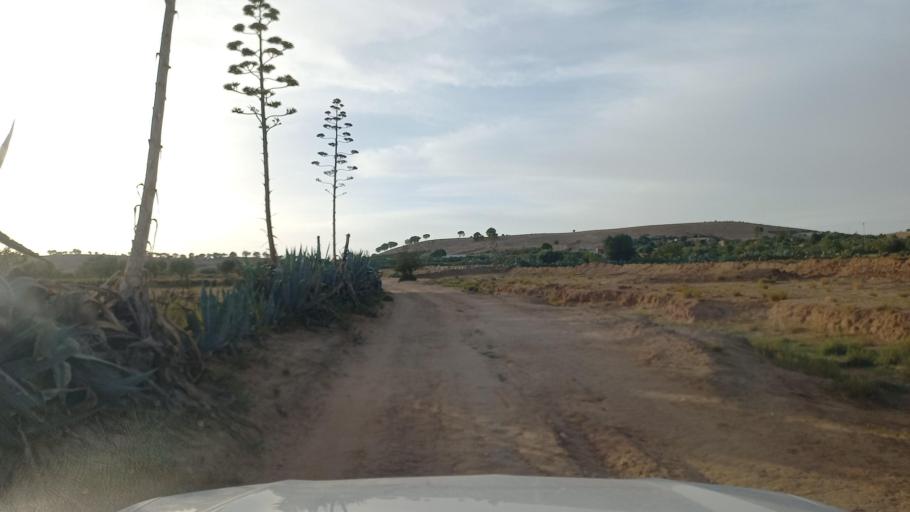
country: TN
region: Al Qasrayn
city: Sbiba
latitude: 35.4083
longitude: 8.9054
